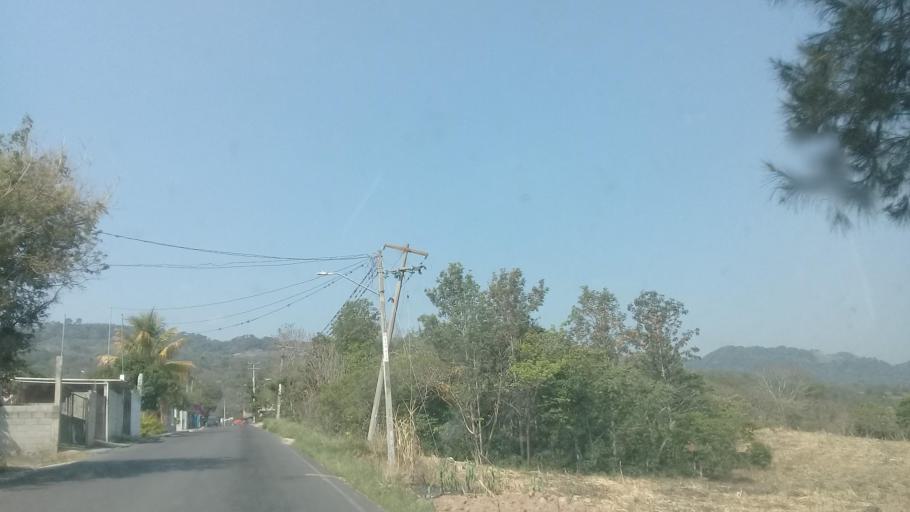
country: MX
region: Veracruz
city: El Castillo
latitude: 19.5728
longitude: -96.8331
